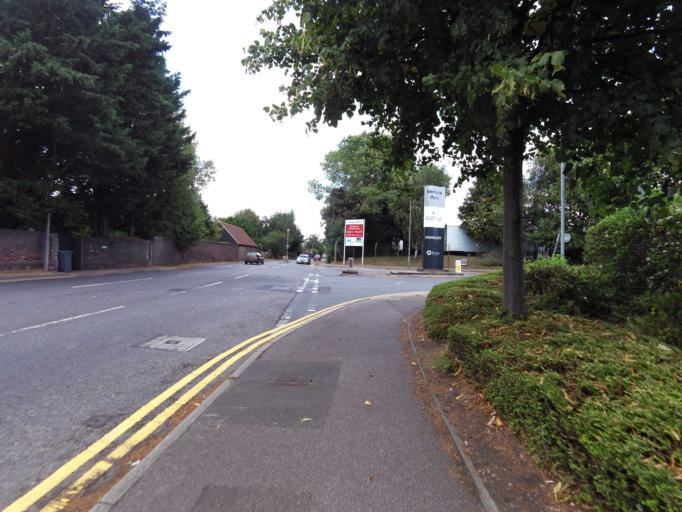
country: GB
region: England
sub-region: Hertfordshire
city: Radlett
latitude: 51.7067
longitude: -0.3297
